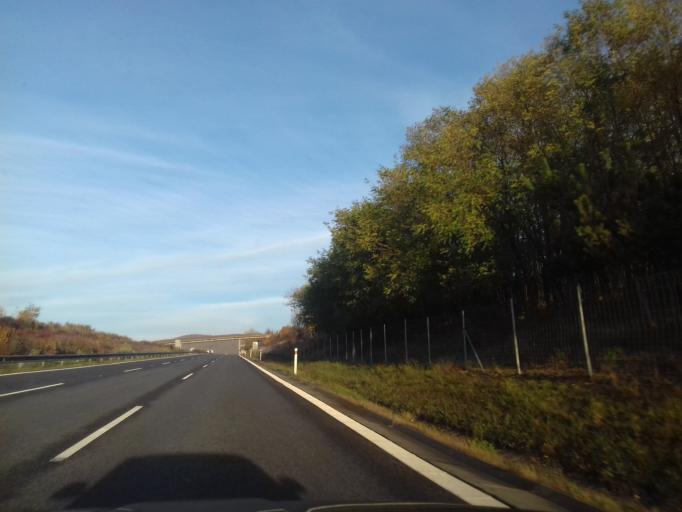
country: SK
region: Nitriansky
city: Tlmace
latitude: 48.3673
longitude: 18.5465
